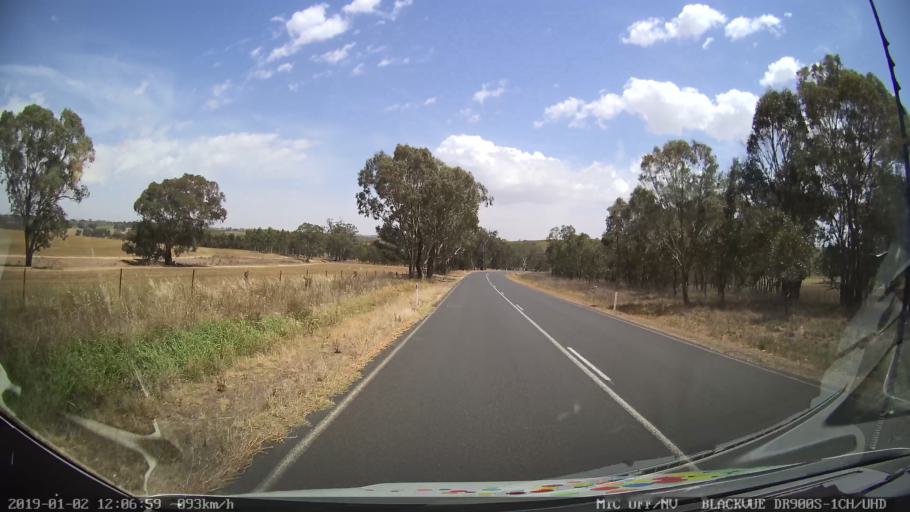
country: AU
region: New South Wales
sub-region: Young
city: Young
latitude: -34.4979
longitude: 148.2891
